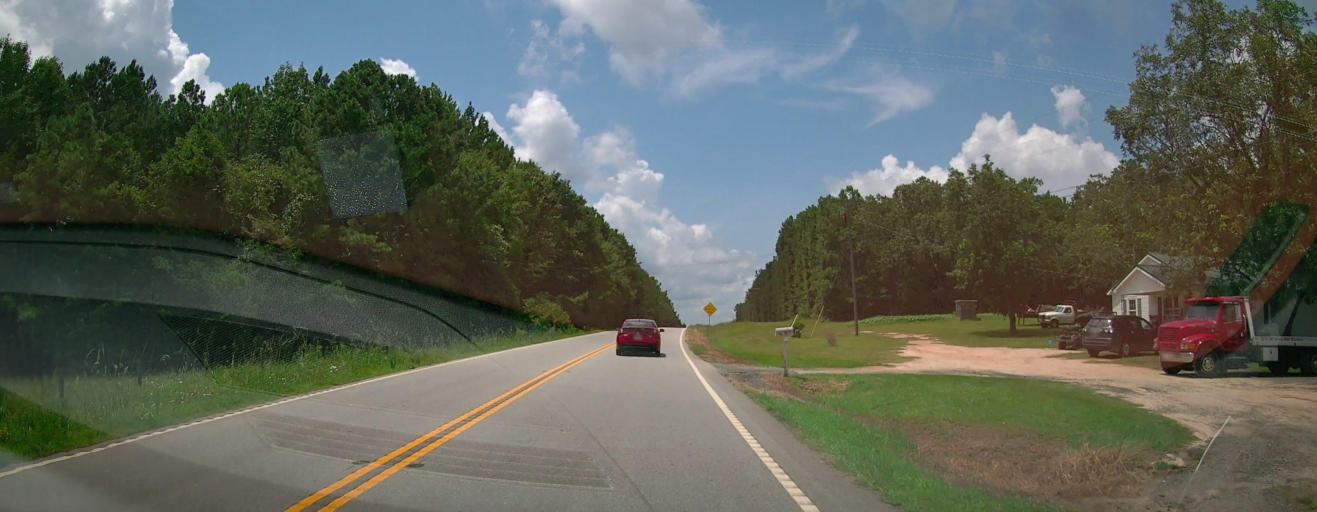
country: US
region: Georgia
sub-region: Meriwether County
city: Greenville
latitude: 32.9887
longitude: -84.6213
